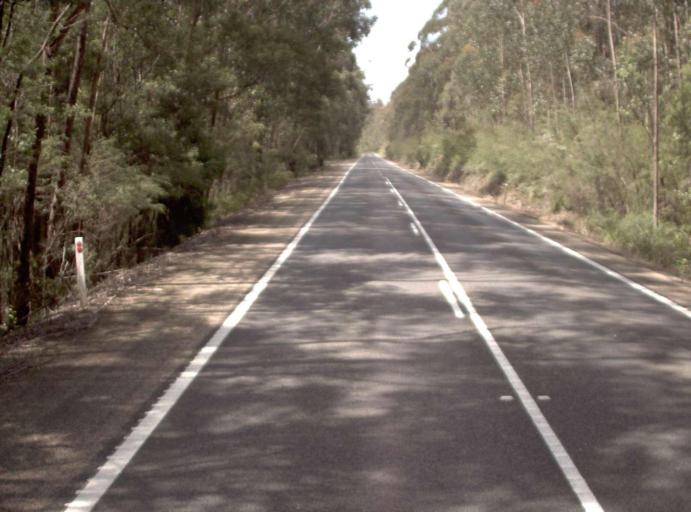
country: AU
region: New South Wales
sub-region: Bombala
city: Bombala
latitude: -37.5472
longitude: 149.3646
